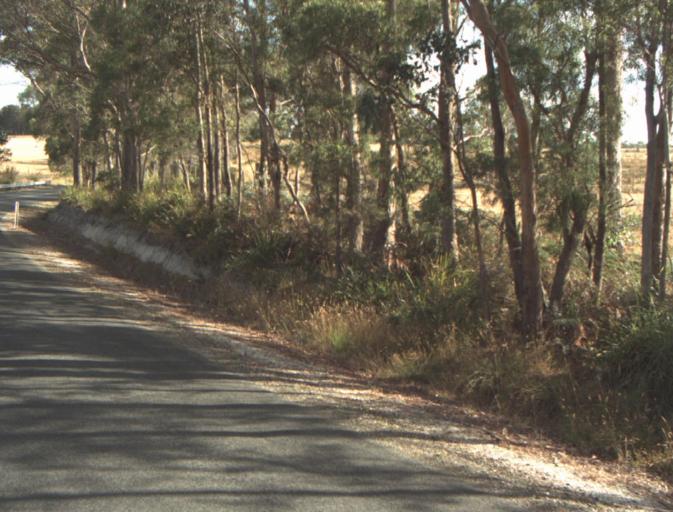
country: AU
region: Tasmania
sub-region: Dorset
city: Bridport
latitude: -41.1133
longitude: 147.2007
